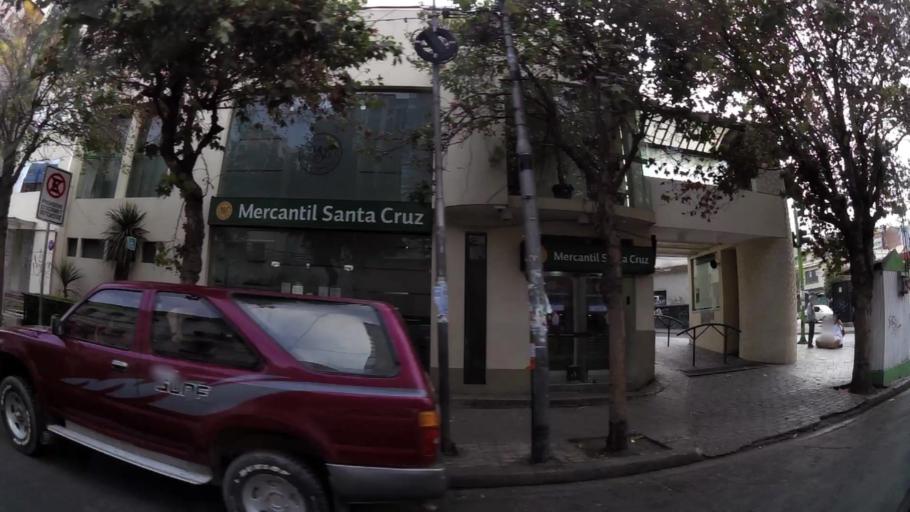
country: BO
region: La Paz
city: La Paz
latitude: -16.5015
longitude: -68.1214
